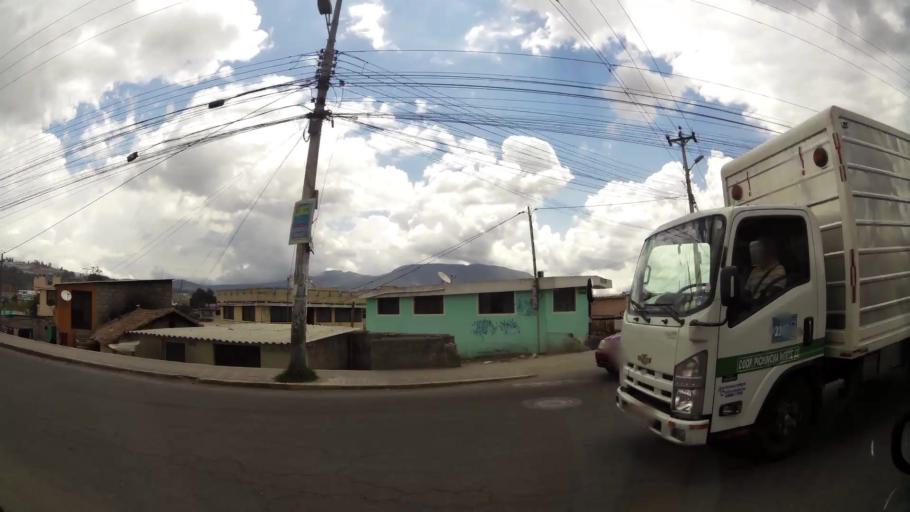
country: EC
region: Pichincha
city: Quito
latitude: -0.0994
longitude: -78.4452
